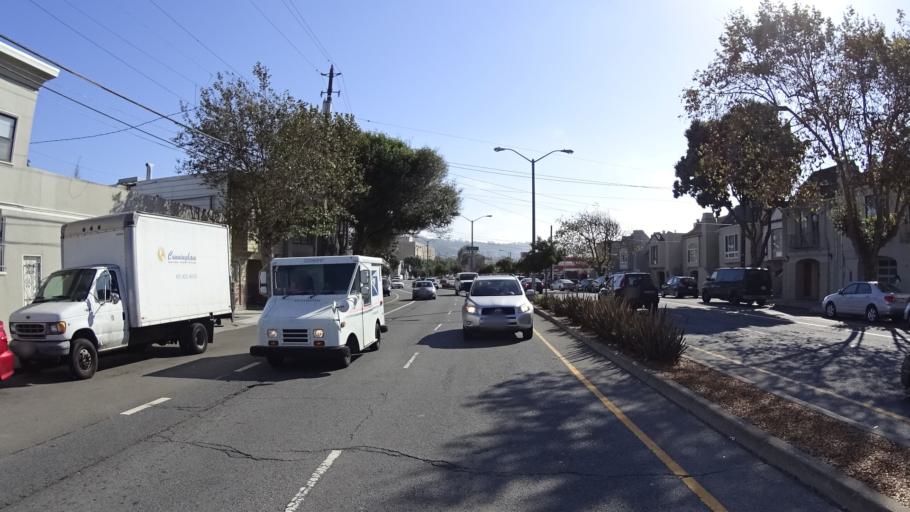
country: US
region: California
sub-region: San Mateo County
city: Daly City
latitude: 37.7247
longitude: -122.4370
